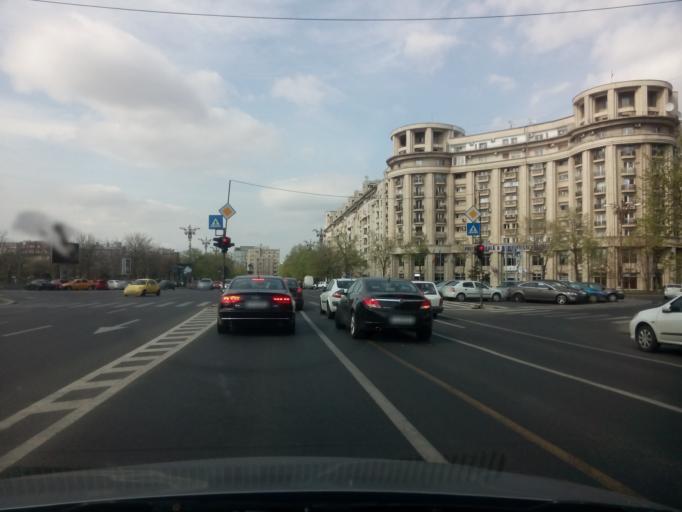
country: RO
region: Bucuresti
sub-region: Municipiul Bucuresti
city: Bucuresti
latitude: 44.4294
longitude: 26.0913
